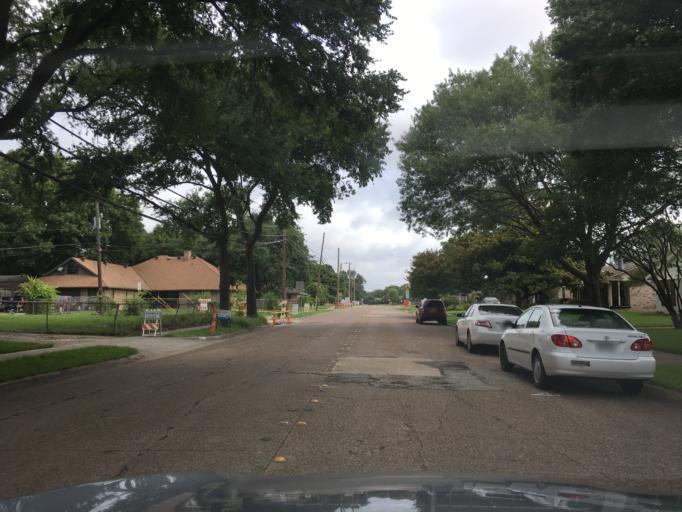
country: US
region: Texas
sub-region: Dallas County
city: Richardson
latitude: 32.9494
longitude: -96.7231
